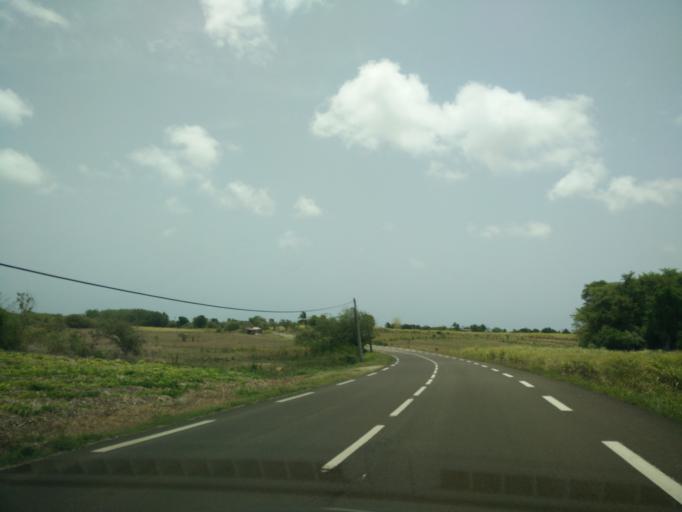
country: GP
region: Guadeloupe
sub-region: Guadeloupe
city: Anse-Bertrand
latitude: 16.4547
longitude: -61.5131
